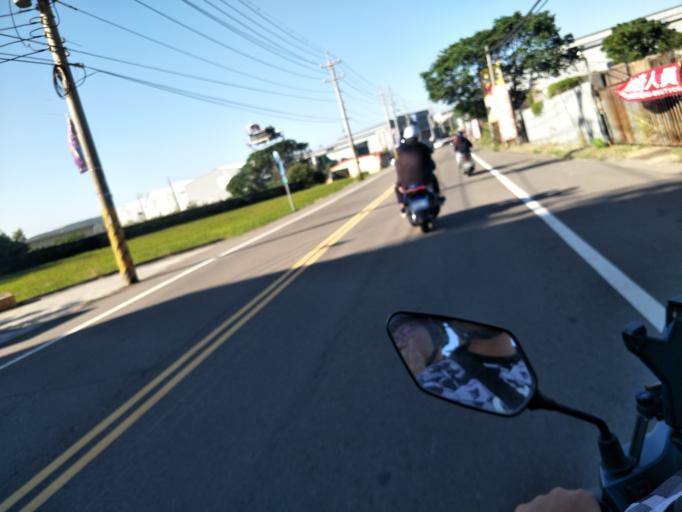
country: TW
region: Taiwan
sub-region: Hsinchu
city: Zhubei
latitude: 24.8335
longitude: 121.0362
